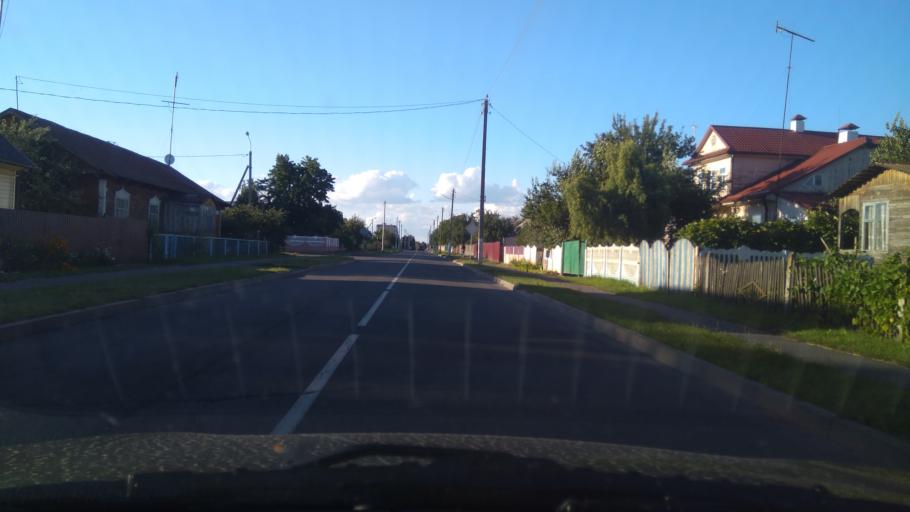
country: BY
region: Brest
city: Pruzhany
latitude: 52.5634
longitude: 24.4630
